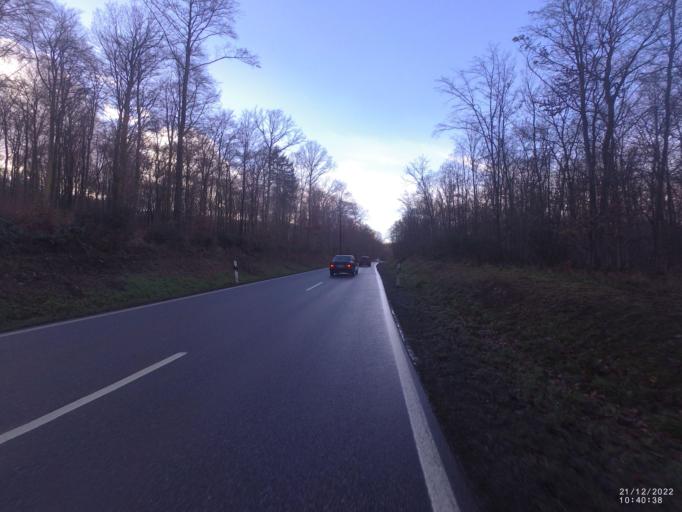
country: DE
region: Rheinland-Pfalz
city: Konigsfeld
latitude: 50.5059
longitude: 7.2015
